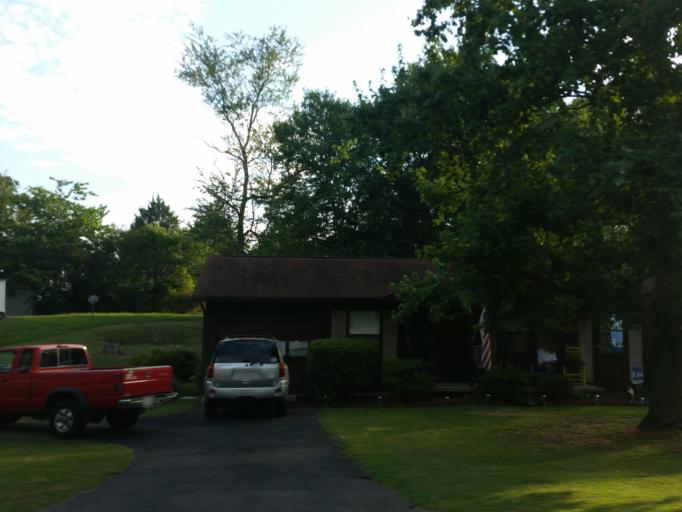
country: US
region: Tennessee
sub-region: Knox County
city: Knoxville
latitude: 36.0434
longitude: -83.9383
